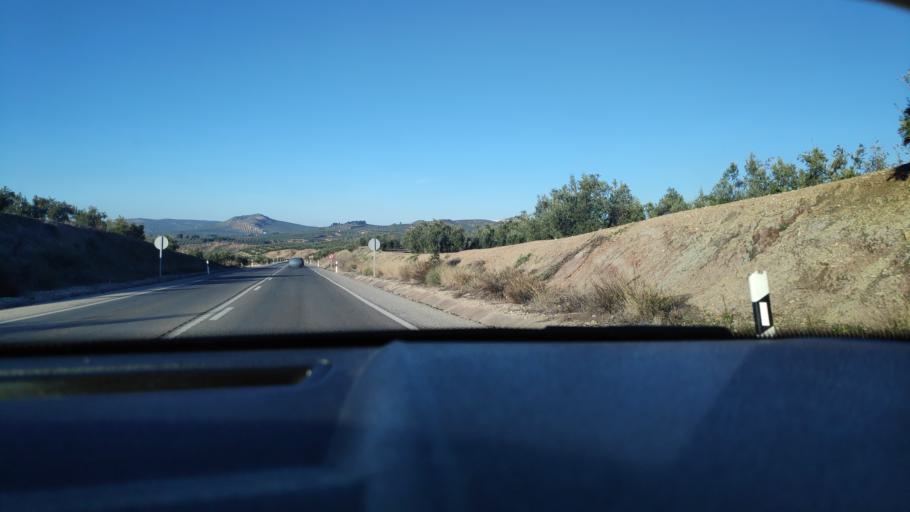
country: ES
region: Andalusia
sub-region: Provincia de Jaen
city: Alcaudete
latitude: 37.6119
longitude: -4.1244
